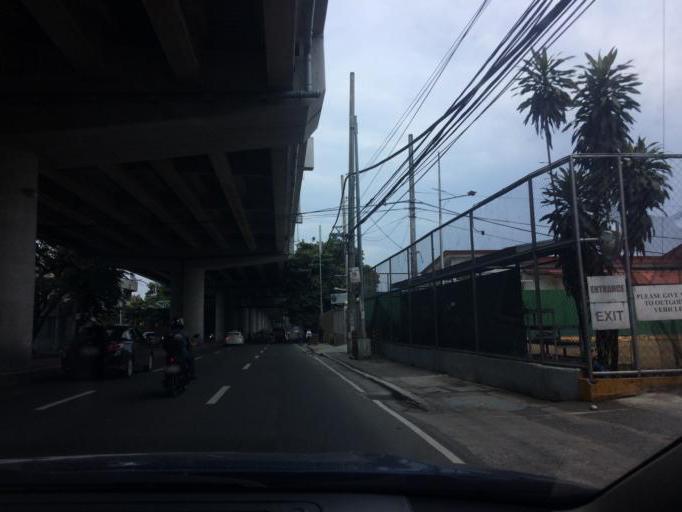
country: PH
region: Metro Manila
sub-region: Makati City
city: Makati City
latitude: 14.5276
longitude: 121.0073
